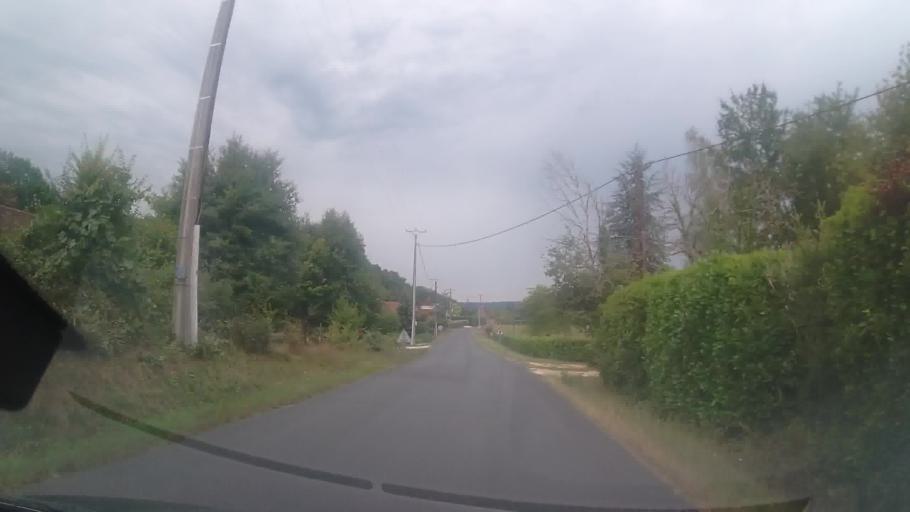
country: FR
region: Aquitaine
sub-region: Departement de la Dordogne
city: Carsac-Aillac
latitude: 44.8379
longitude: 1.2861
